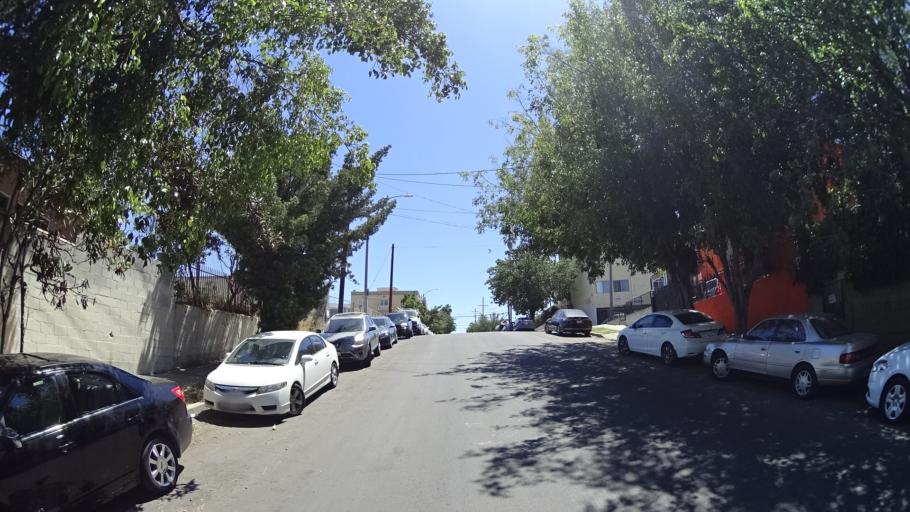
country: US
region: California
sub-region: Los Angeles County
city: Echo Park
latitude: 34.0686
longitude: -118.2671
